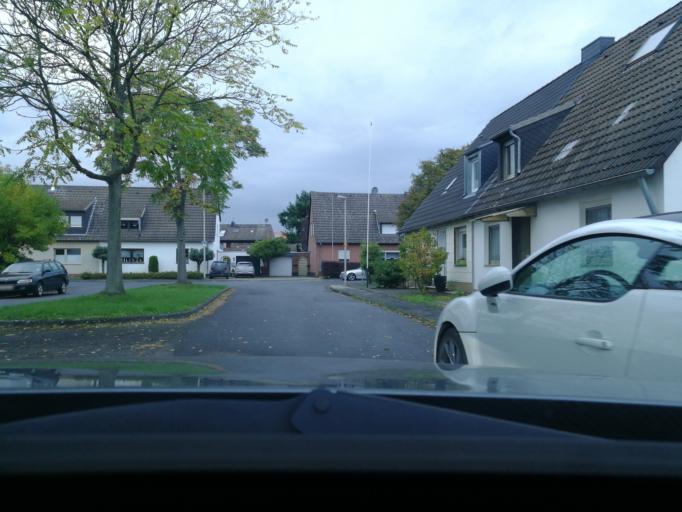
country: DE
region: North Rhine-Westphalia
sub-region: Regierungsbezirk Dusseldorf
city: Dormagen
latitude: 51.1176
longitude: 6.7665
